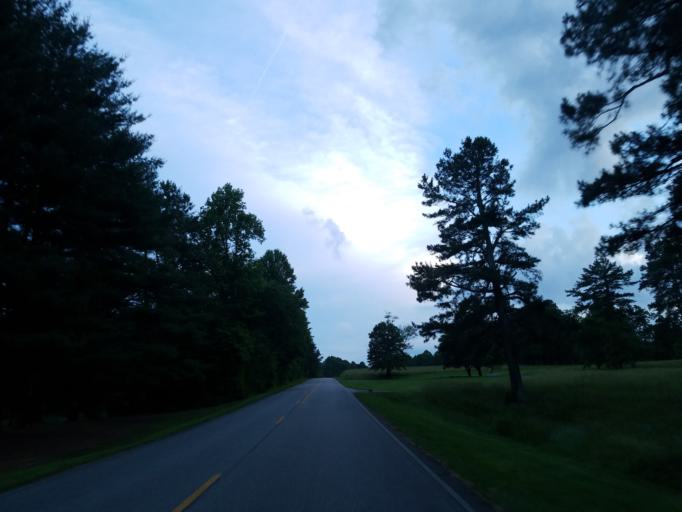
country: US
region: Georgia
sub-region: Dawson County
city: Dawsonville
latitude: 34.4791
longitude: -84.1744
